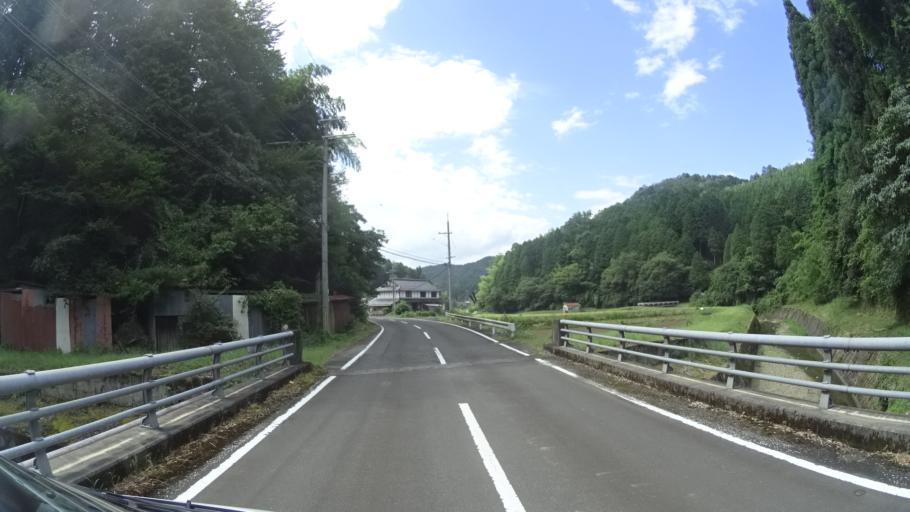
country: JP
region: Kyoto
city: Fukuchiyama
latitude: 35.3676
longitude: 135.1628
